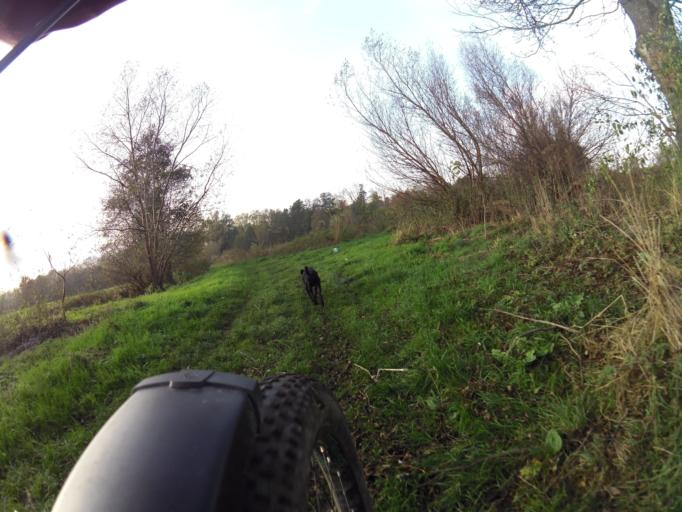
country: PL
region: Pomeranian Voivodeship
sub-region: Powiat pucki
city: Krokowa
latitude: 54.7760
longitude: 18.1679
